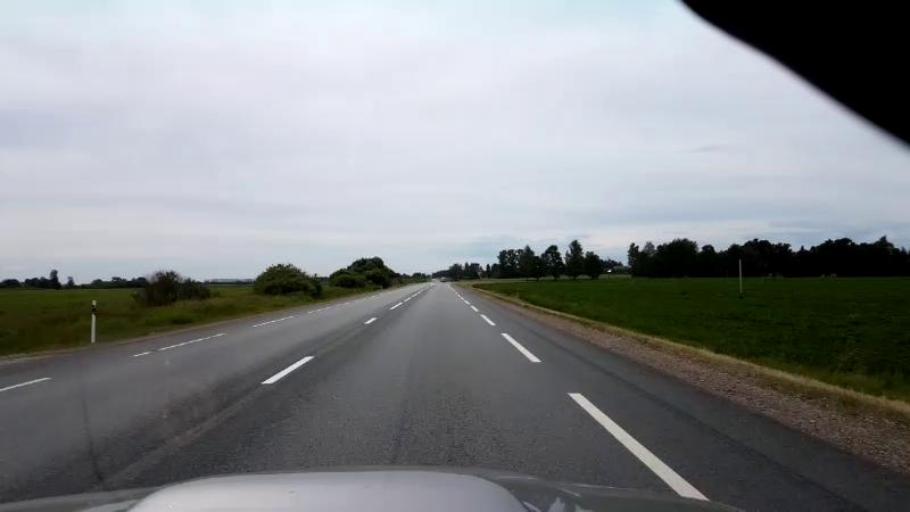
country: LV
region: Lecava
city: Iecava
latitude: 56.5696
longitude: 24.1755
